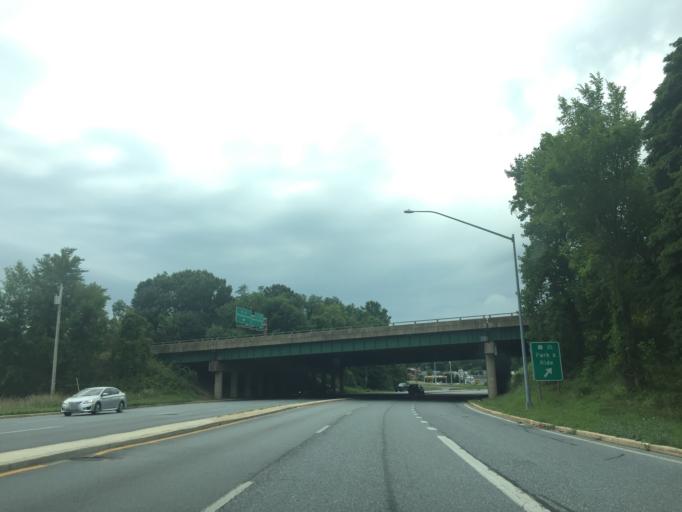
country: US
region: Maryland
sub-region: Baltimore County
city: Woodlawn
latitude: 39.3022
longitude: -76.7124
